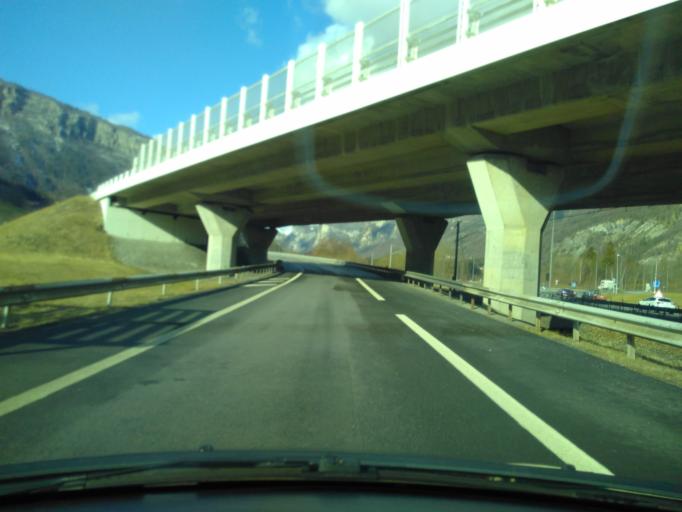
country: FR
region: Rhone-Alpes
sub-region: Departement de la Haute-Savoie
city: Sallanches
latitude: 45.9631
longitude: 6.6294
